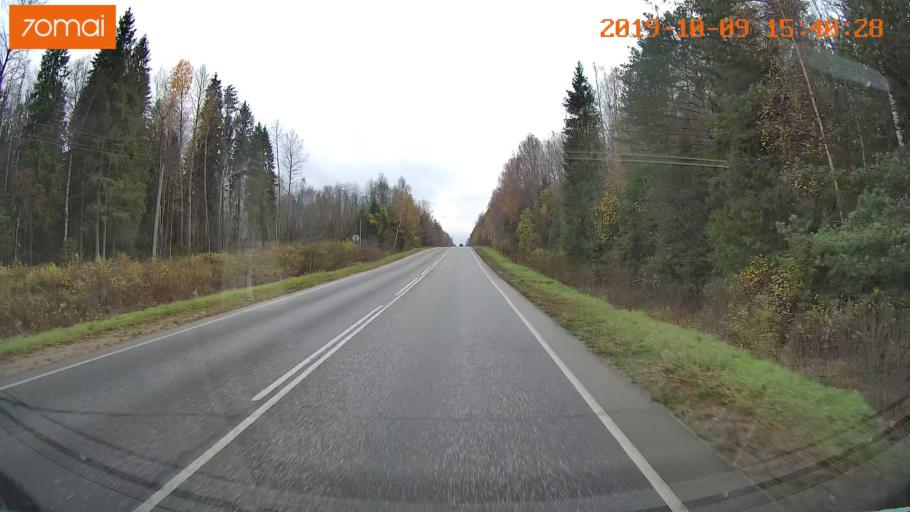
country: RU
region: Kostroma
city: Oktyabr'skiy
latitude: 57.8873
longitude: 41.1437
